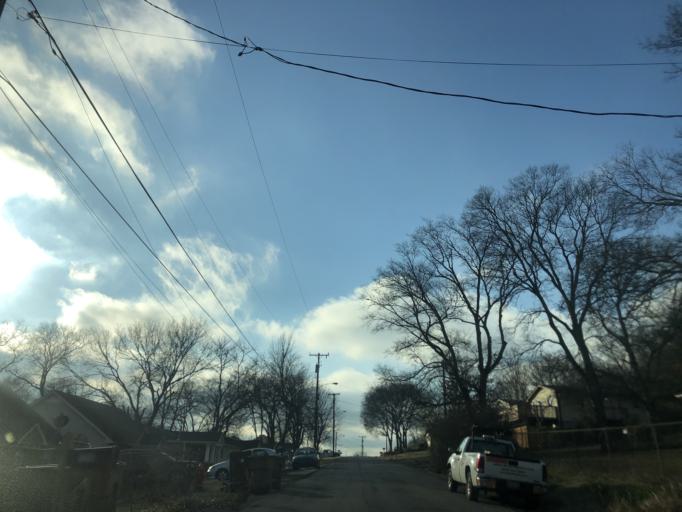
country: US
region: Tennessee
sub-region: Davidson County
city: Nashville
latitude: 36.2097
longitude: -86.7805
